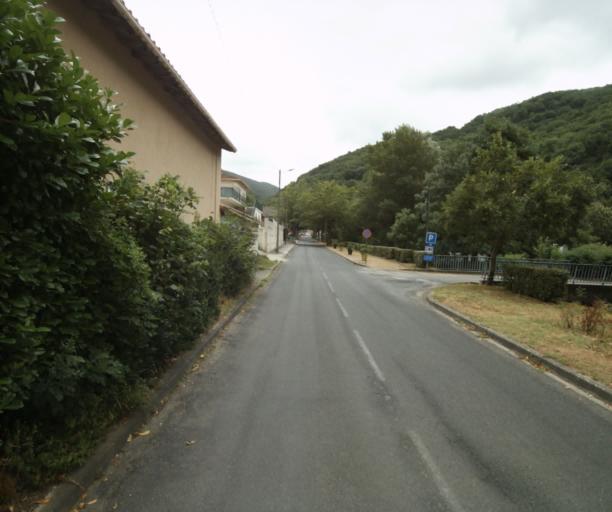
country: FR
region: Midi-Pyrenees
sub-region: Departement du Tarn
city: Soreze
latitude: 43.4401
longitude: 2.0646
